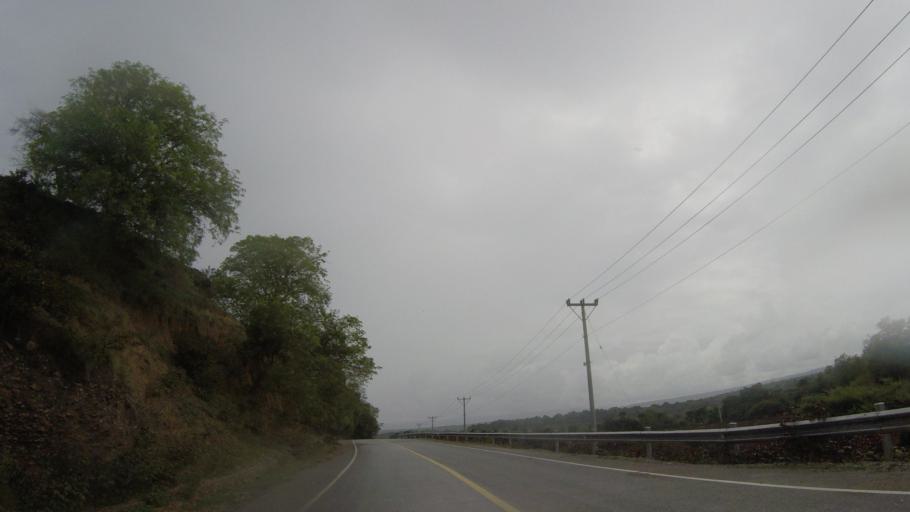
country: TL
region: Lautem
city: Lospalos
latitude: -8.4033
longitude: 126.8281
